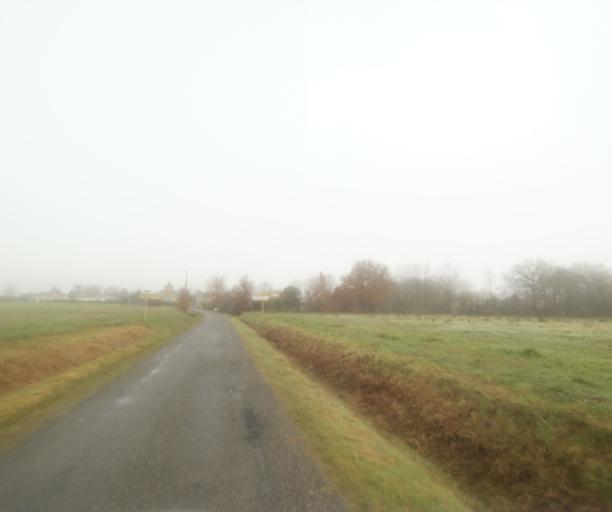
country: FR
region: Midi-Pyrenees
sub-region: Departement de la Haute-Garonne
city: Villaudric
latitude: 43.8382
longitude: 1.4577
